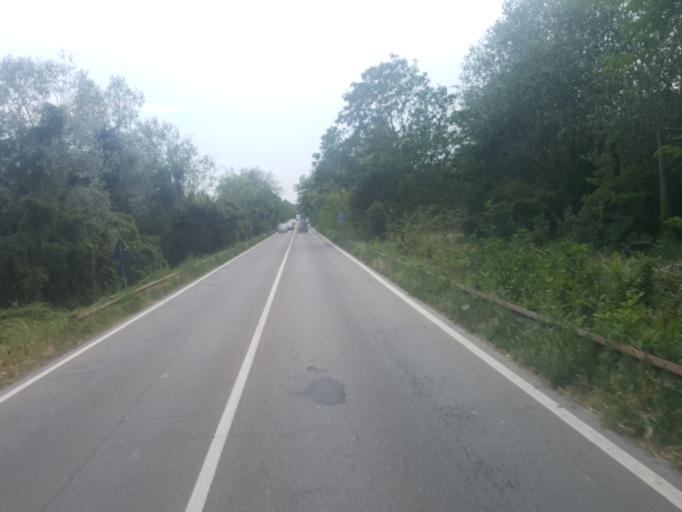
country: IT
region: Emilia-Romagna
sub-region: Provincia di Modena
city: Gaggio
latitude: 44.6220
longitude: 10.9956
